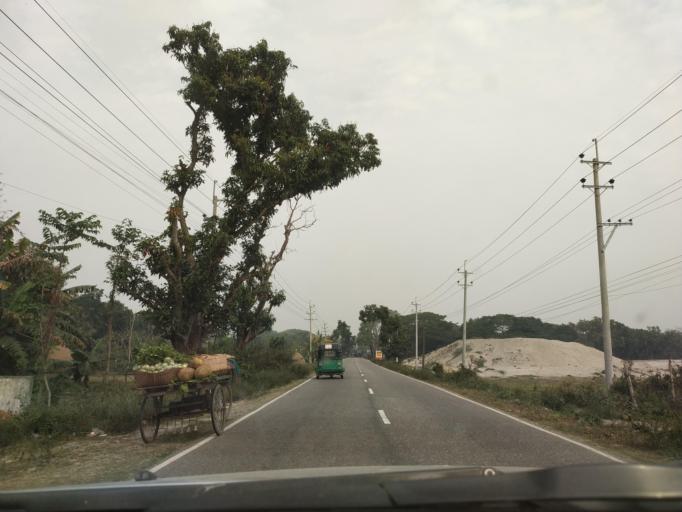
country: BD
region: Dhaka
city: Narsingdi
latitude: 24.0104
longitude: 90.7373
